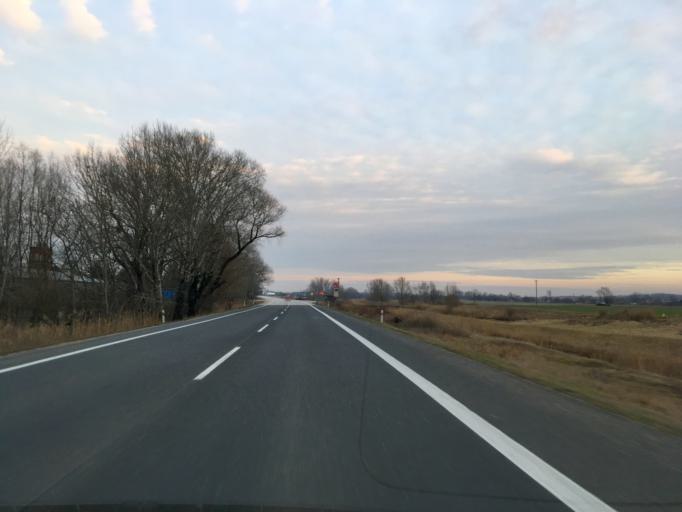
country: HU
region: Komarom-Esztergom
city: Acs
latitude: 47.7677
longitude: 17.9666
